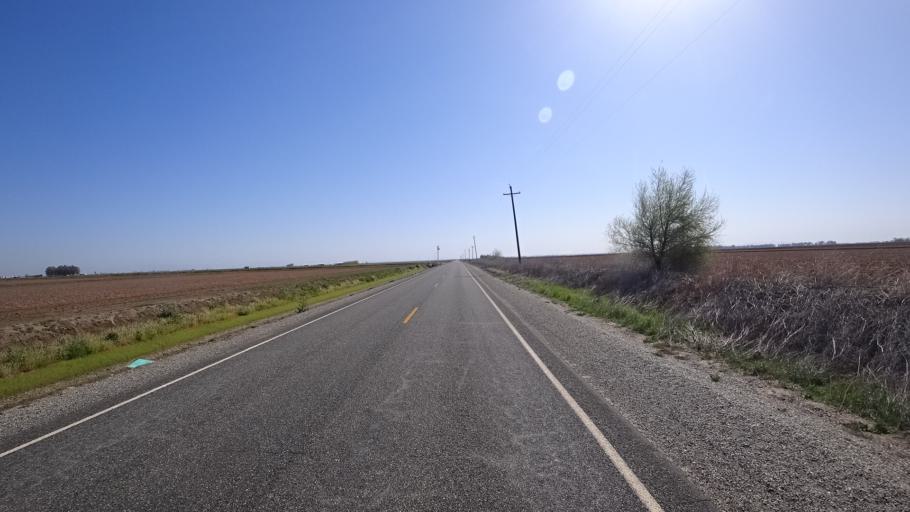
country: US
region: California
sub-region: Glenn County
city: Willows
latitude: 39.4656
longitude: -122.1484
